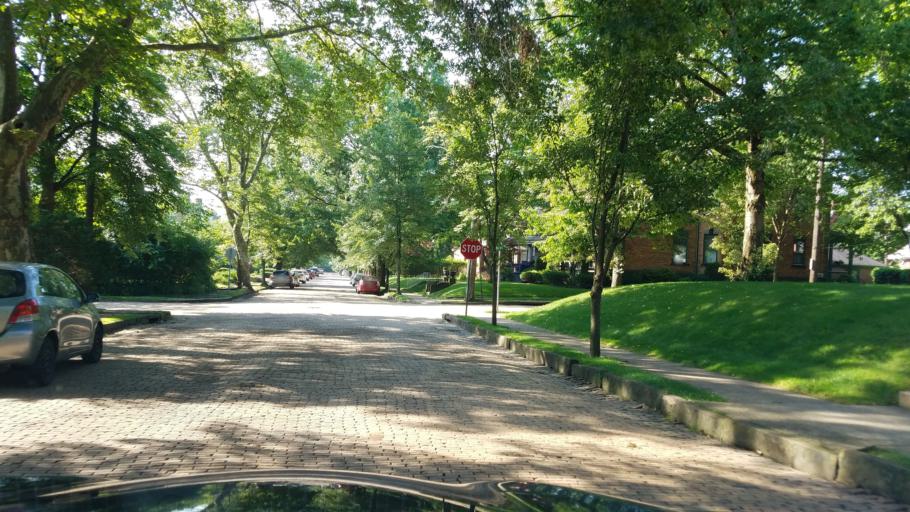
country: US
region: Pennsylvania
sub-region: Allegheny County
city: Edgewood
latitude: 40.4314
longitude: -79.8955
